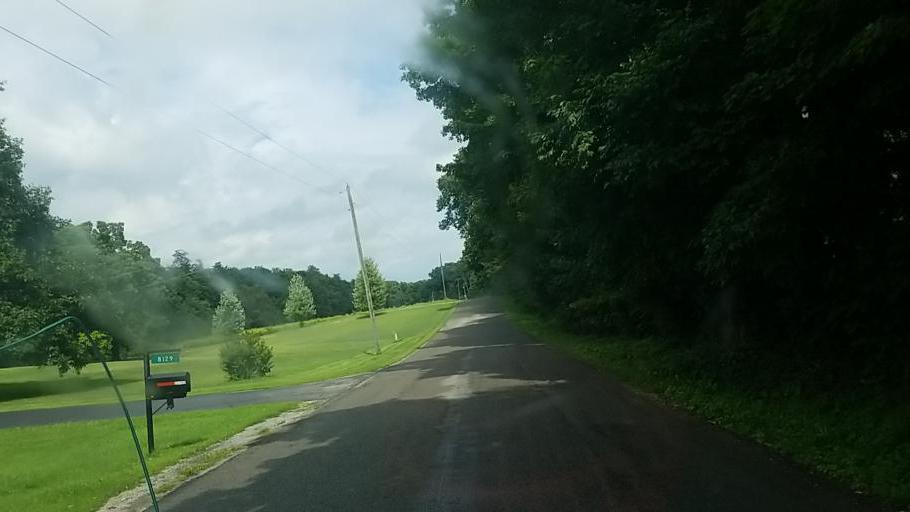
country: US
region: Ohio
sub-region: Champaign County
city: North Lewisburg
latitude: 40.2673
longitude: -83.6091
